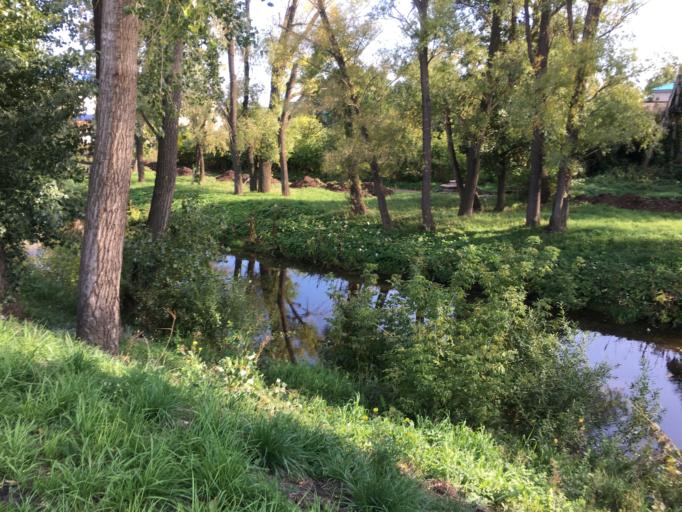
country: RU
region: Bashkortostan
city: Meleuz
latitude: 52.9602
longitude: 55.9314
